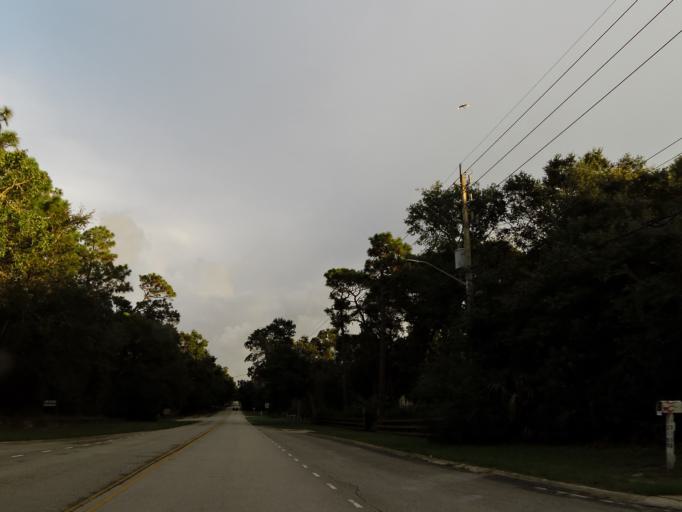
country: US
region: Florida
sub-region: Duval County
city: Atlantic Beach
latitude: 30.3706
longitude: -81.4865
